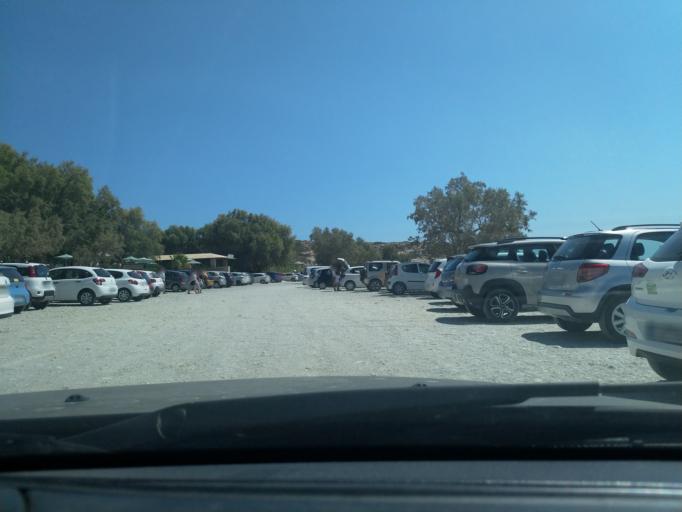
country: GR
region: Crete
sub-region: Nomos Rethymnis
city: Agia Galini
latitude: 35.1192
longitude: 24.5466
